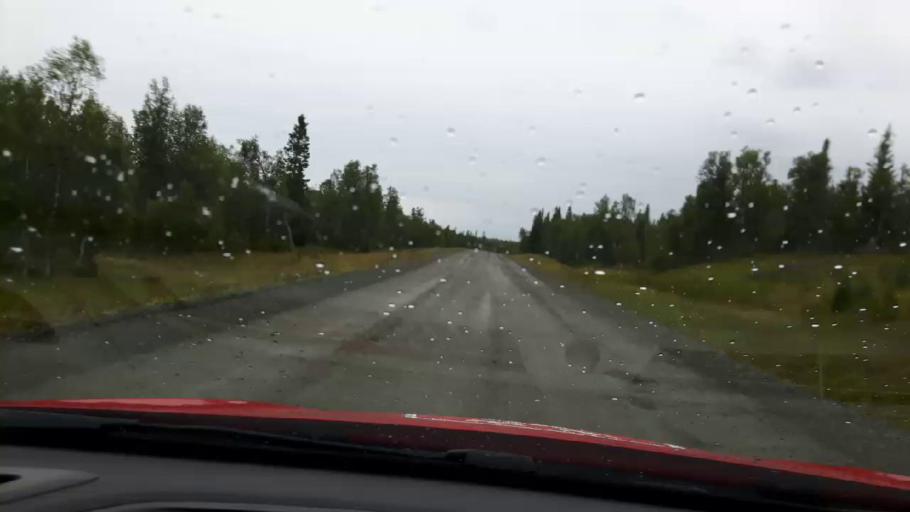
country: NO
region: Nord-Trondelag
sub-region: Meraker
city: Meraker
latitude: 63.5634
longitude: 12.2887
